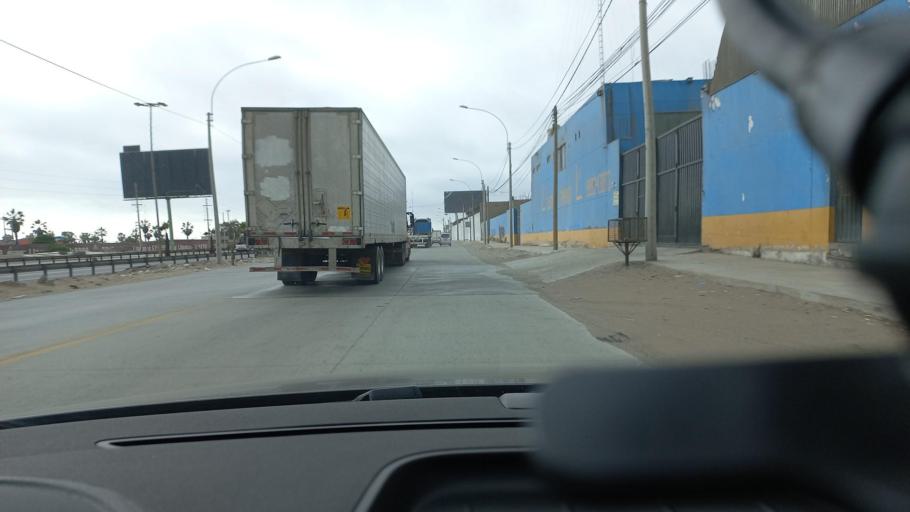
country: PE
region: Lima
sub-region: Lima
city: Surco
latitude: -12.2353
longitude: -76.9571
